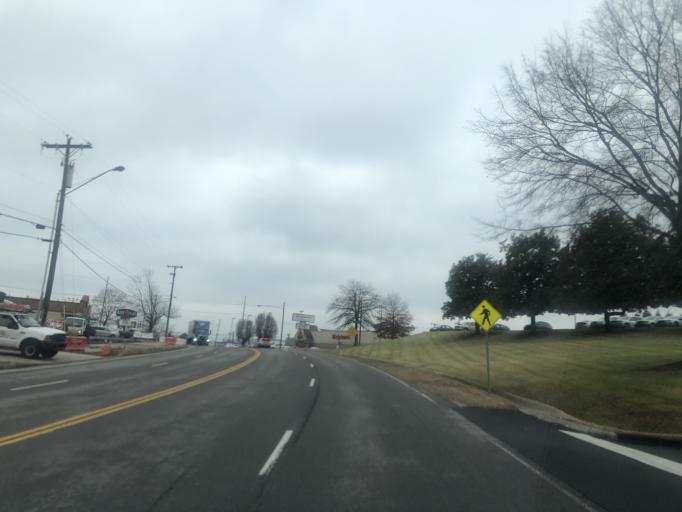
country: US
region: Tennessee
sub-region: Davidson County
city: Lakewood
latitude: 36.1495
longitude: -86.6688
